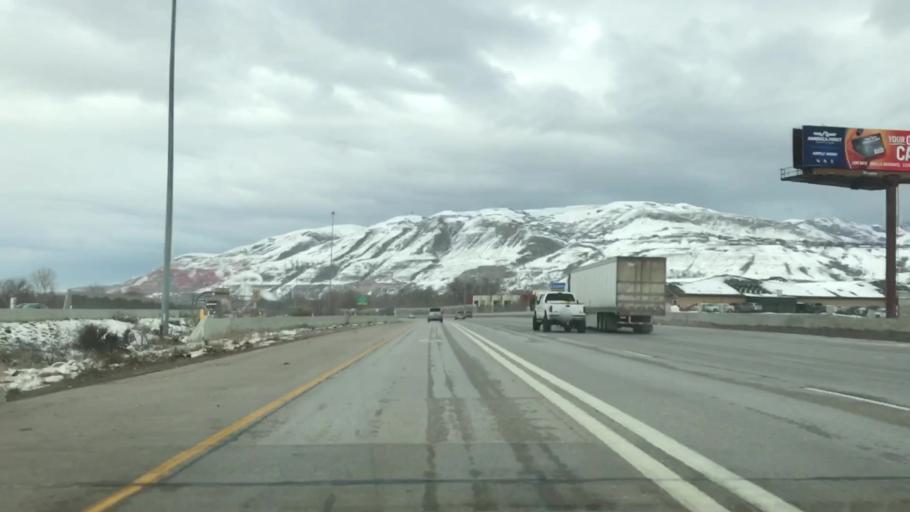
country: US
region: Utah
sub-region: Salt Lake County
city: Salt Lake City
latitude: 40.7695
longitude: -111.9113
